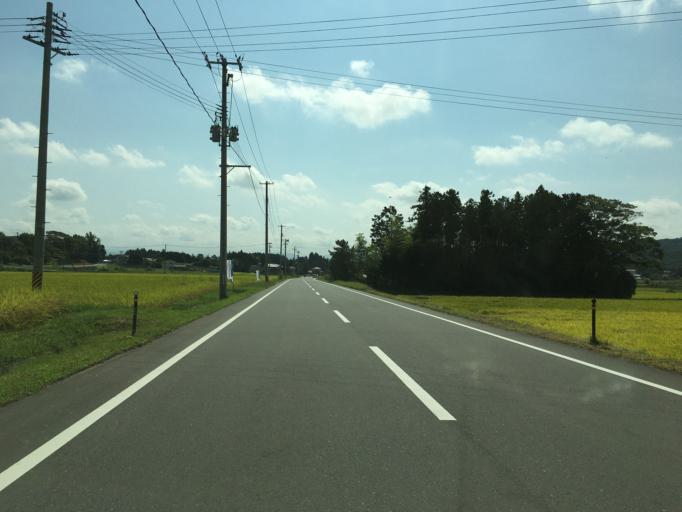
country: JP
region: Fukushima
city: Motomiya
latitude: 37.5380
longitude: 140.3579
